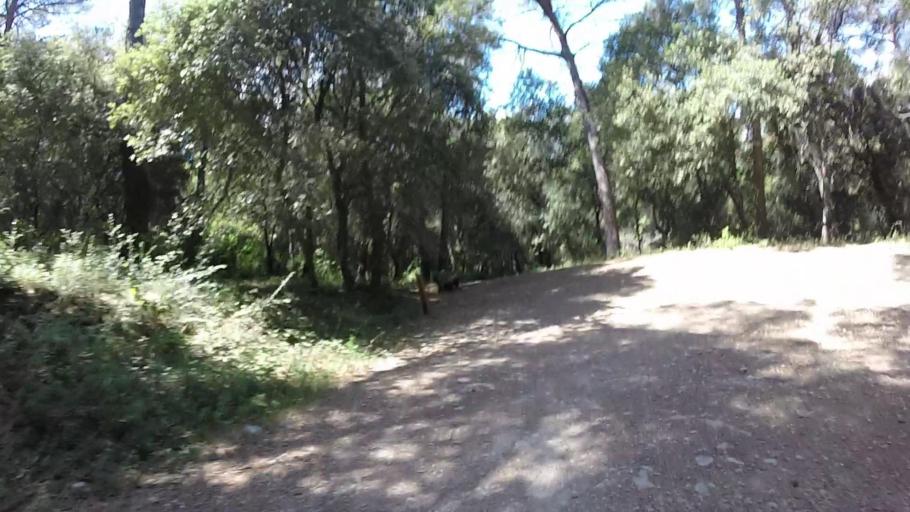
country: FR
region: Provence-Alpes-Cote d'Azur
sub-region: Departement des Alpes-Maritimes
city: Mougins
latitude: 43.6006
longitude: 7.0219
